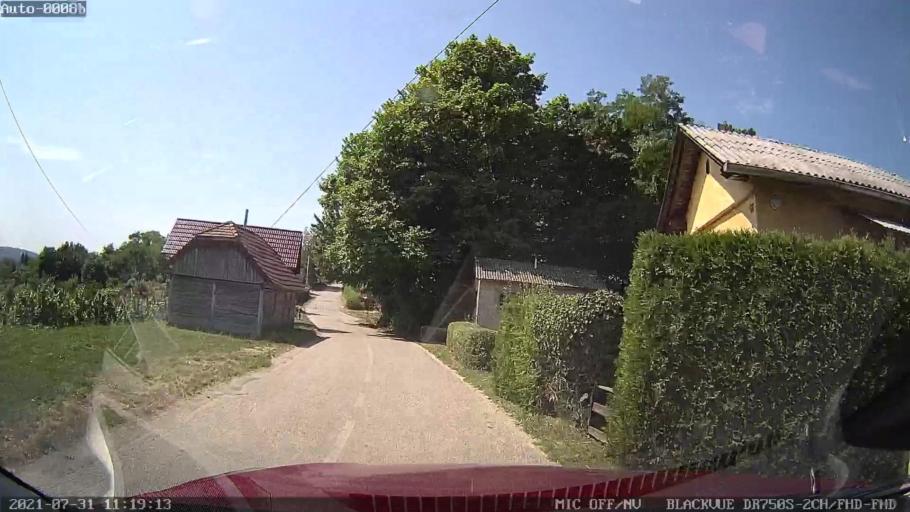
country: HR
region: Varazdinska
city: Jalzabet
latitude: 46.2409
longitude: 16.4740
